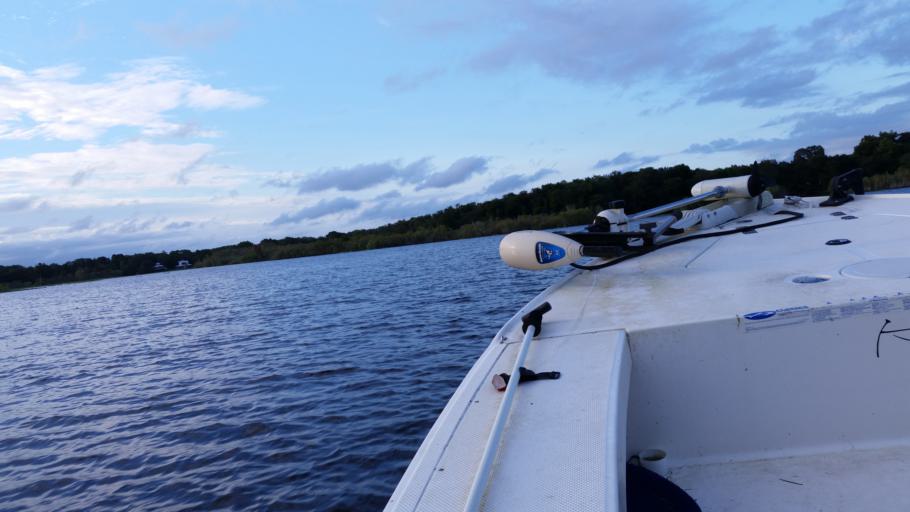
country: US
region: Florida
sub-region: Citrus County
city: Inverness
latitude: 28.8221
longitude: -82.2894
